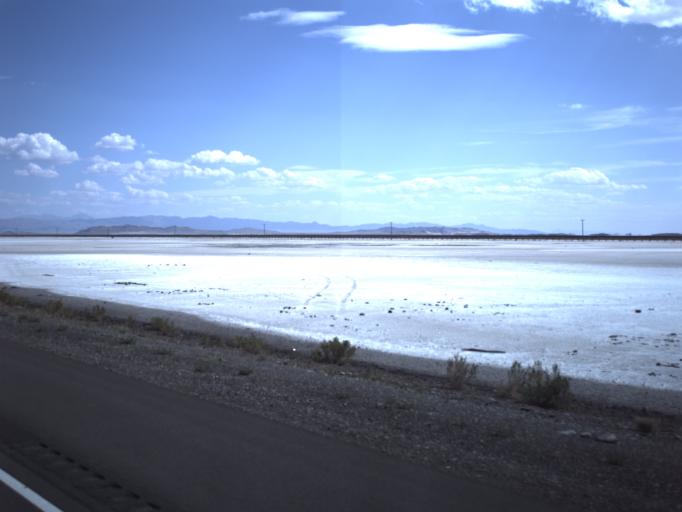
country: US
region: Utah
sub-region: Tooele County
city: Wendover
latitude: 40.7294
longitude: -113.4374
